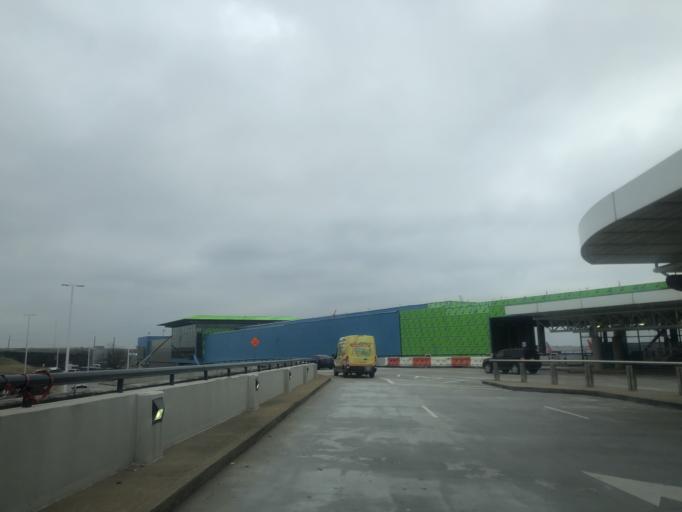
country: US
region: Tennessee
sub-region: Davidson County
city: Lakewood
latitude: 36.1312
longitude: -86.6684
